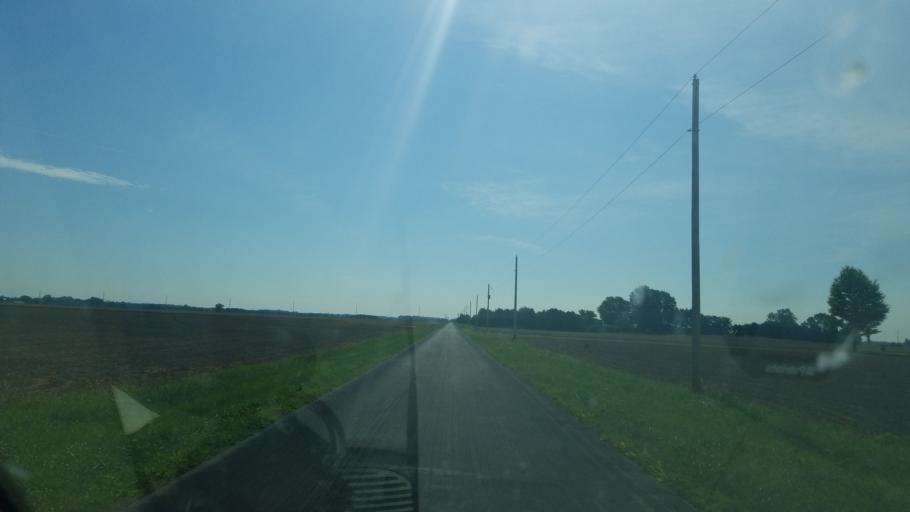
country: US
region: Ohio
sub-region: Wyandot County
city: Carey
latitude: 40.9781
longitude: -83.3147
